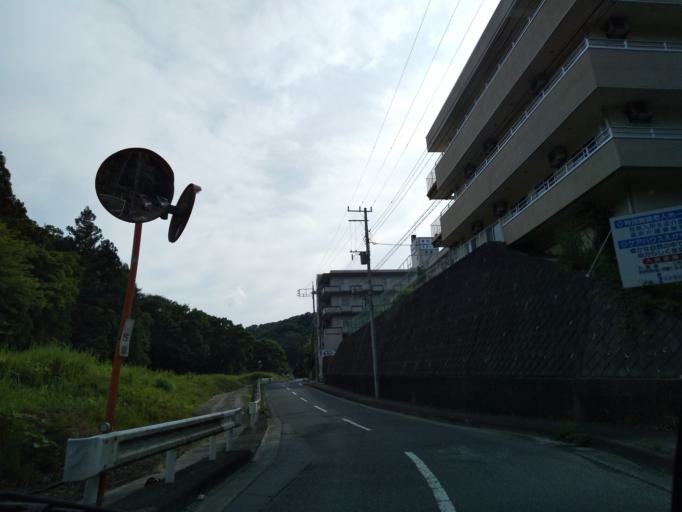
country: JP
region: Kanagawa
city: Atsugi
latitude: 35.4885
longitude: 139.3092
